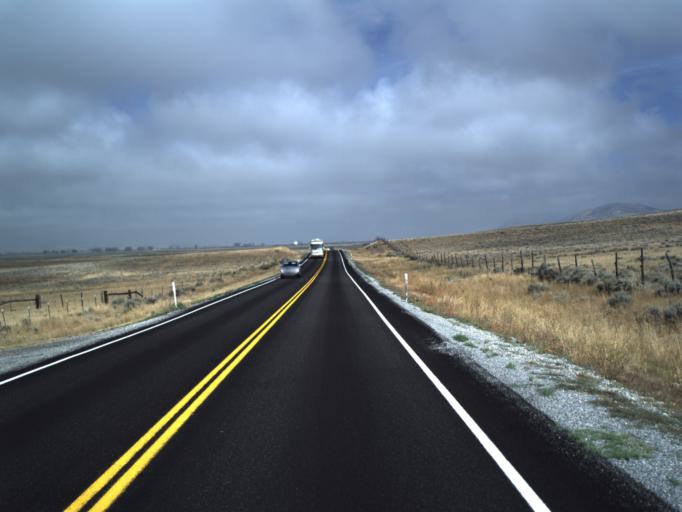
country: US
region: Utah
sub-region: Rich County
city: Randolph
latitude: 41.4828
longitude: -111.1162
